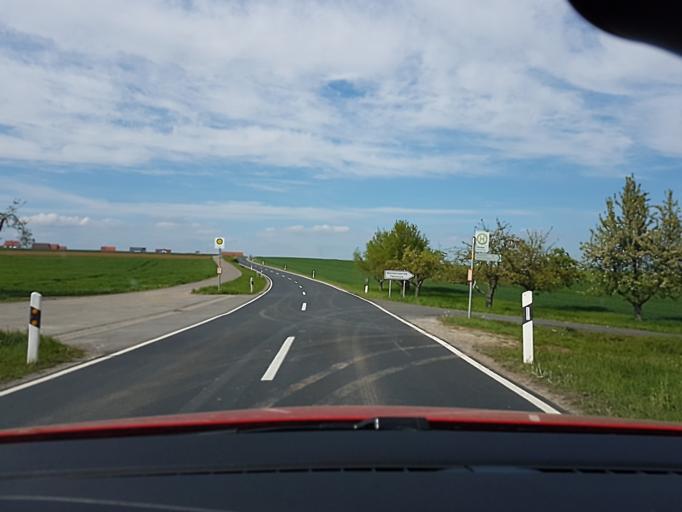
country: DE
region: Bavaria
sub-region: Regierungsbezirk Unterfranken
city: Bergtheim
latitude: 49.9186
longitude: 10.0273
